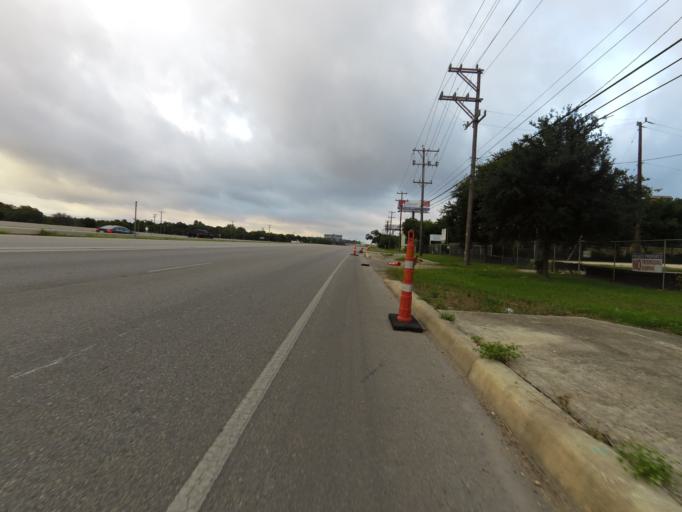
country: US
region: Texas
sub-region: Bexar County
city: Cross Mountain
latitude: 29.6351
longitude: -98.6142
